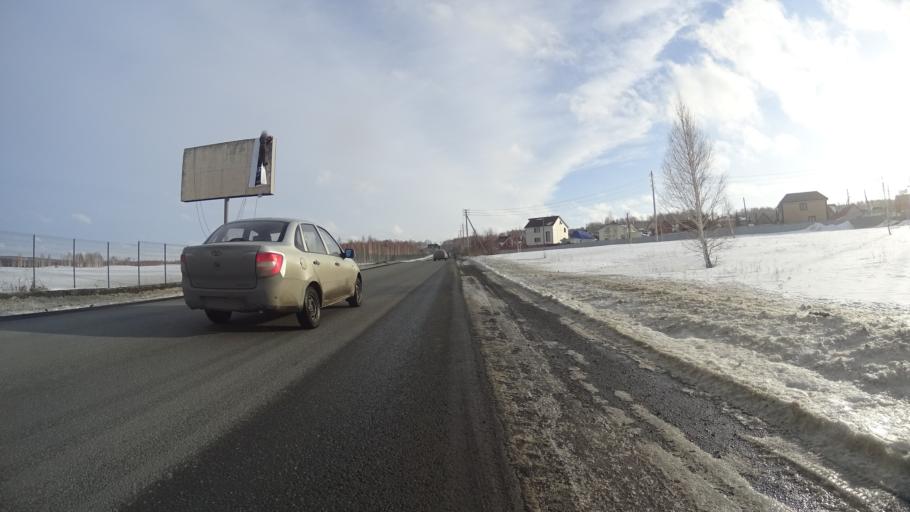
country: RU
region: Chelyabinsk
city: Sargazy
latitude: 55.1336
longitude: 61.2861
